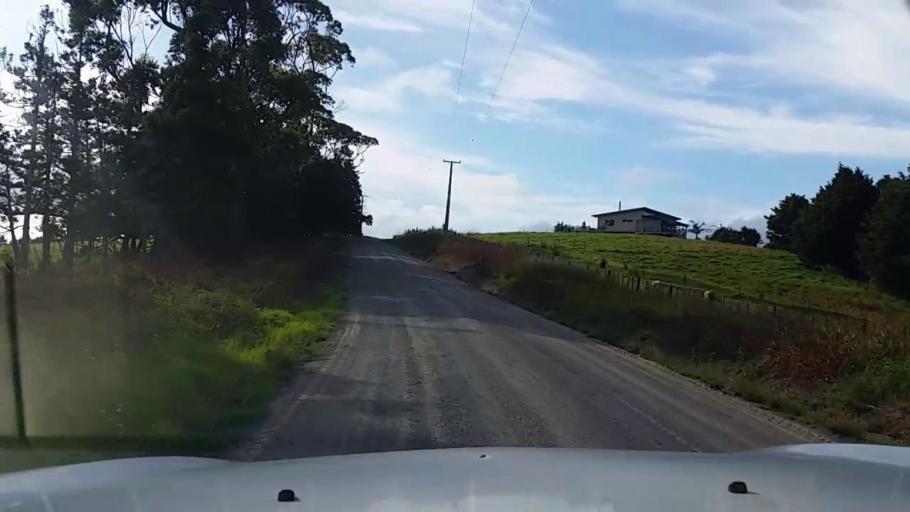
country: NZ
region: Northland
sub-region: Whangarei
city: Maungatapere
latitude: -35.6728
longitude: 174.1755
